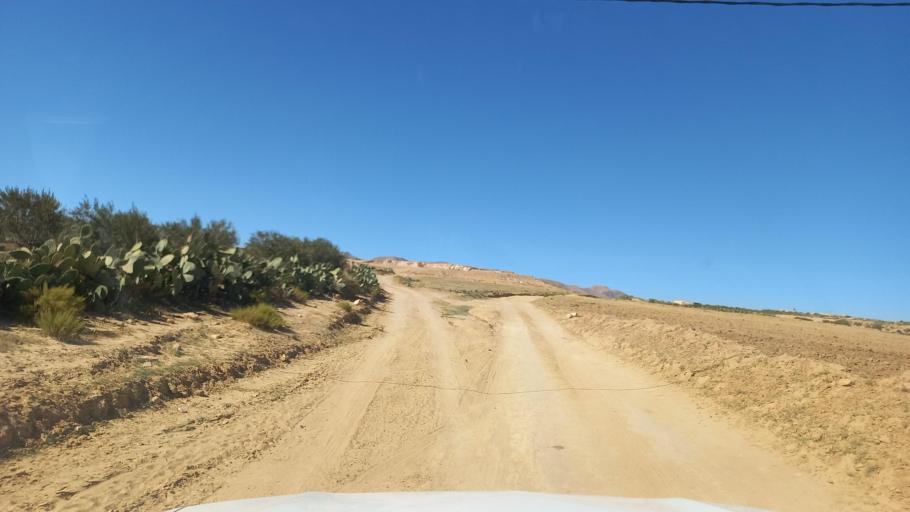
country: TN
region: Al Qasrayn
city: Sbiba
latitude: 35.3770
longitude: 9.0913
